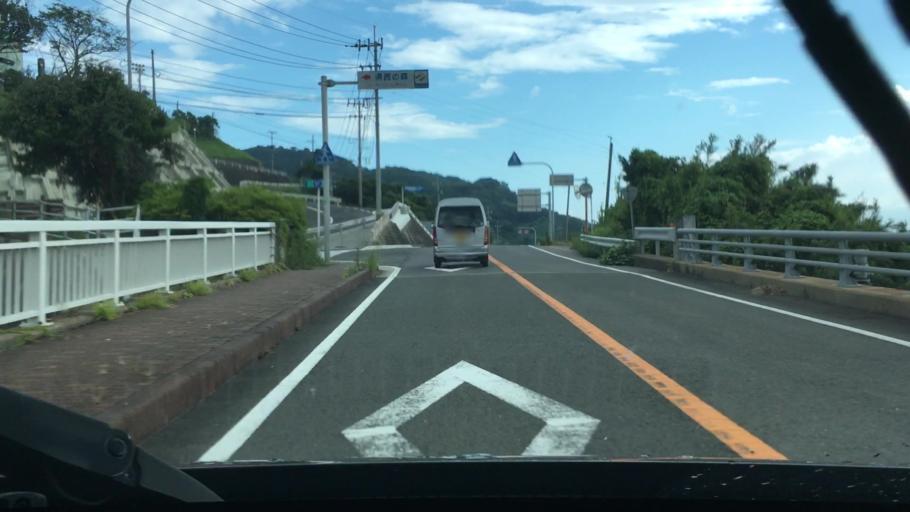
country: JP
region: Nagasaki
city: Togitsu
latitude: 32.8789
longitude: 129.6801
